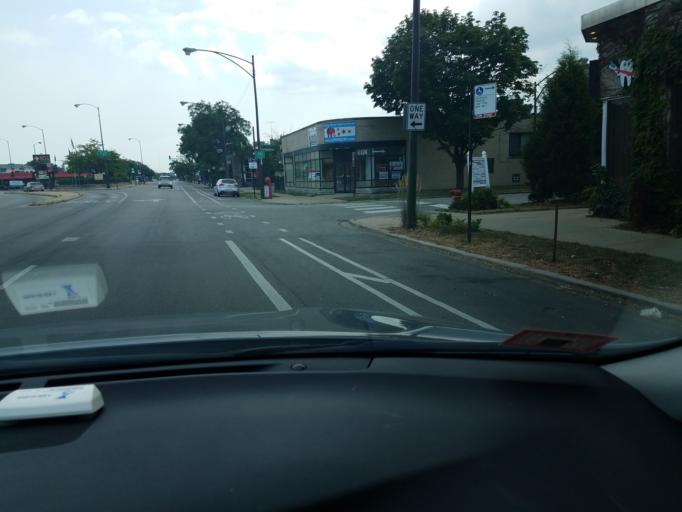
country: US
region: Illinois
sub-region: Cook County
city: Niles
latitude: 41.9932
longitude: -87.7841
